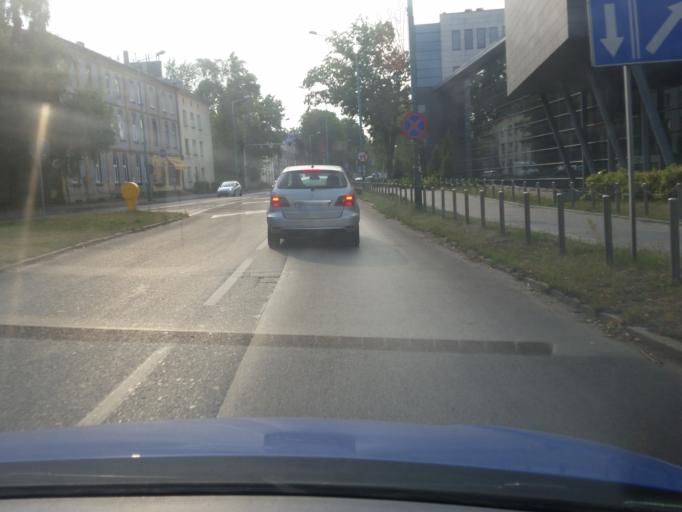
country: PL
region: Silesian Voivodeship
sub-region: Sosnowiec
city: Sosnowiec
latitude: 50.2855
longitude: 19.1305
